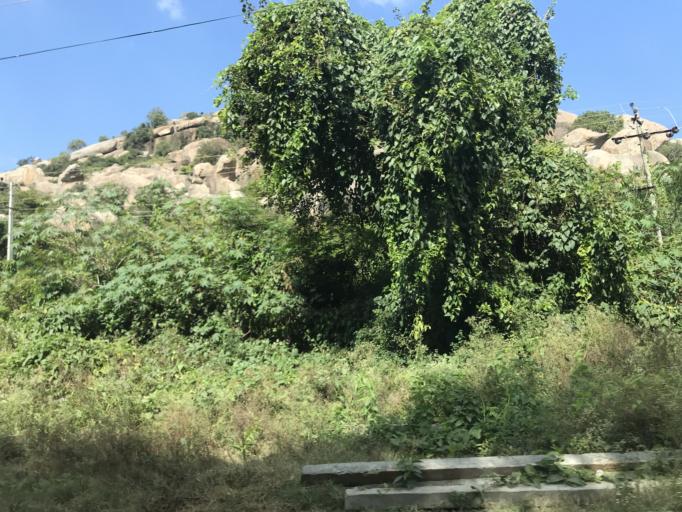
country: IN
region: Karnataka
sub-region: Hassan
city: Shravanabelagola
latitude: 12.8516
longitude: 76.4835
